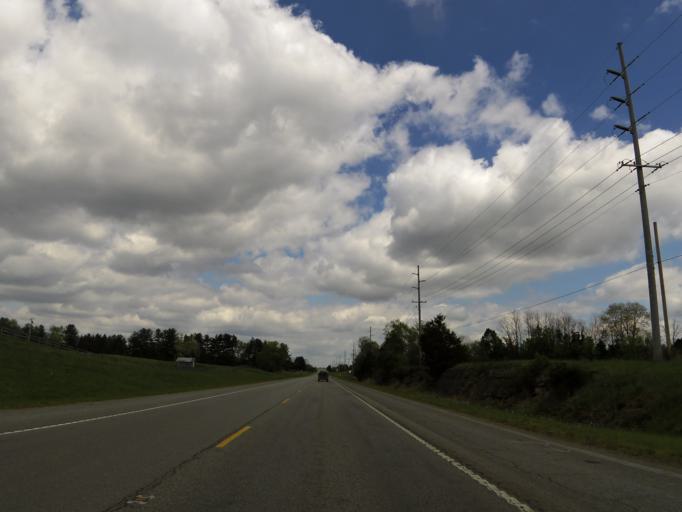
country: US
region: Kentucky
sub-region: Bell County
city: Middlesboro
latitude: 36.5117
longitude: -83.7815
